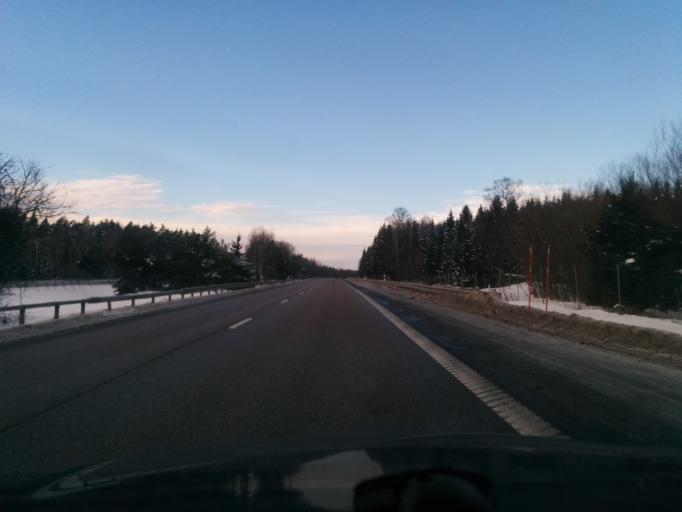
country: SE
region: Stockholm
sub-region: Upplands-Bro Kommun
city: Bro
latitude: 59.5414
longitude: 17.6120
